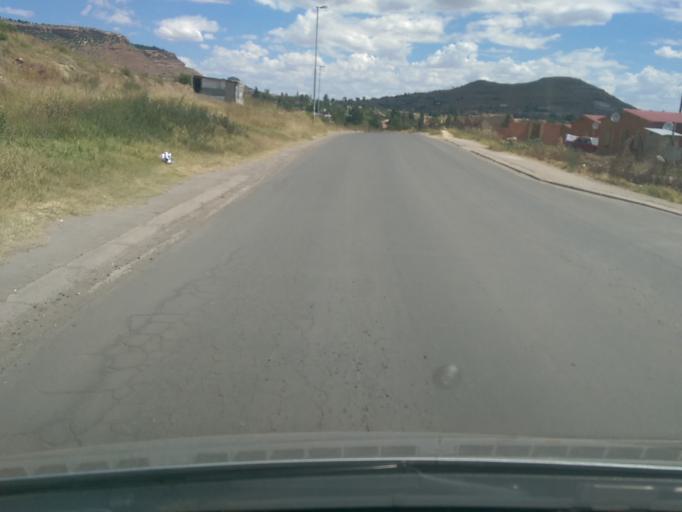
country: LS
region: Maseru
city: Maseru
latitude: -29.3203
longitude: 27.4835
